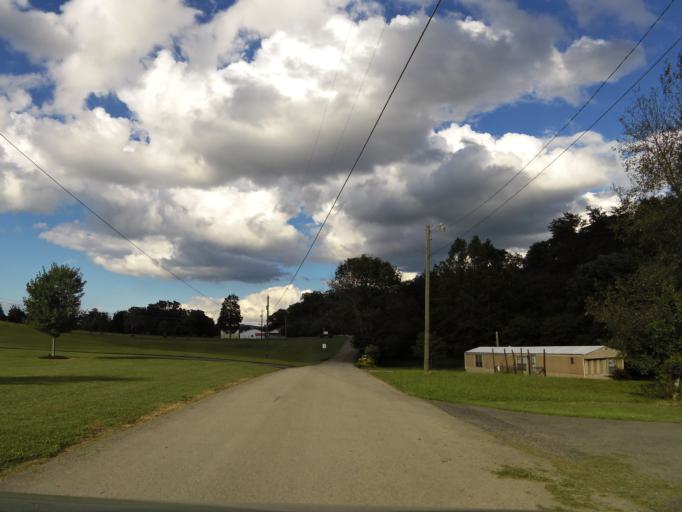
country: US
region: Tennessee
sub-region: Knox County
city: Mascot
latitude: 36.1099
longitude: -83.7839
